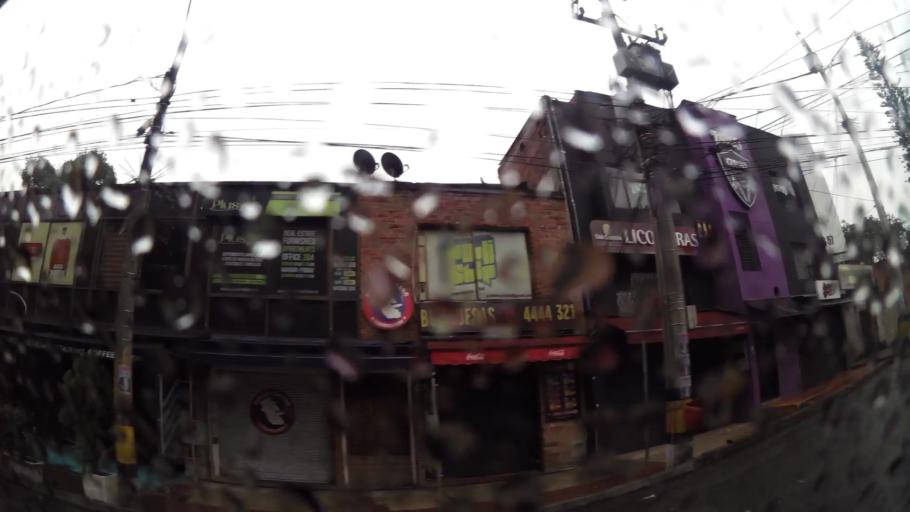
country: CO
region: Antioquia
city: Itagui
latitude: 6.2089
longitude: -75.5682
